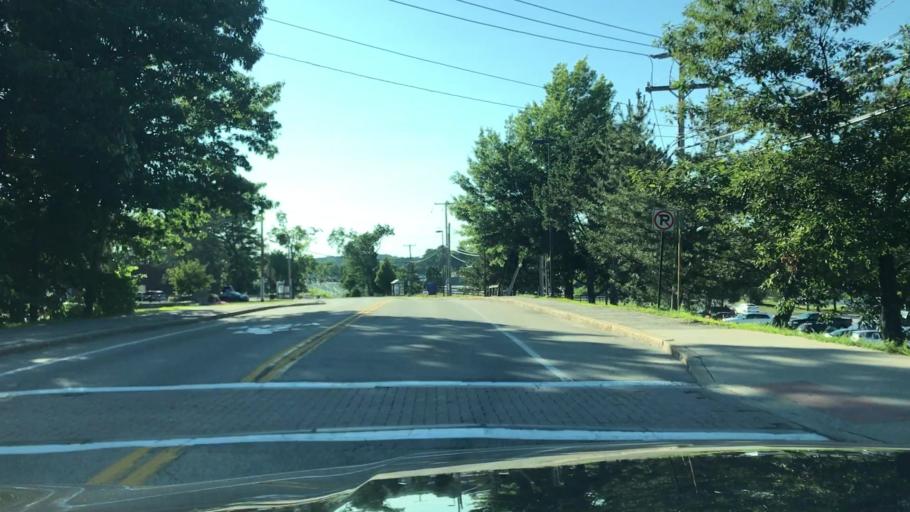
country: US
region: New Hampshire
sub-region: Strafford County
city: Durham
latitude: 43.1391
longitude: -70.9366
